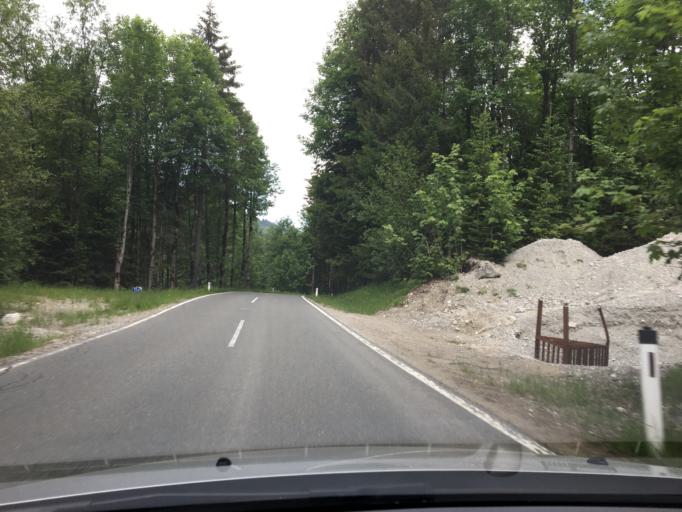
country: AT
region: Salzburg
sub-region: Politischer Bezirk Sankt Johann im Pongau
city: Kleinarl
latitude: 47.2450
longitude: 13.3289
